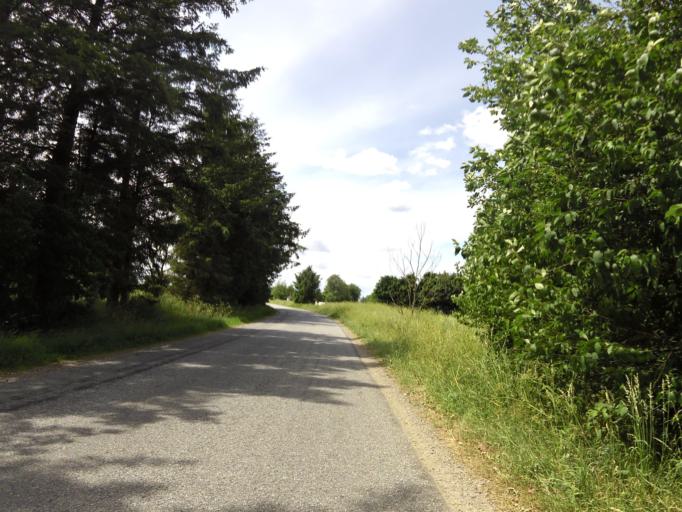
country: DK
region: South Denmark
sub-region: Esbjerg Kommune
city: Ribe
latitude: 55.2630
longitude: 8.8788
